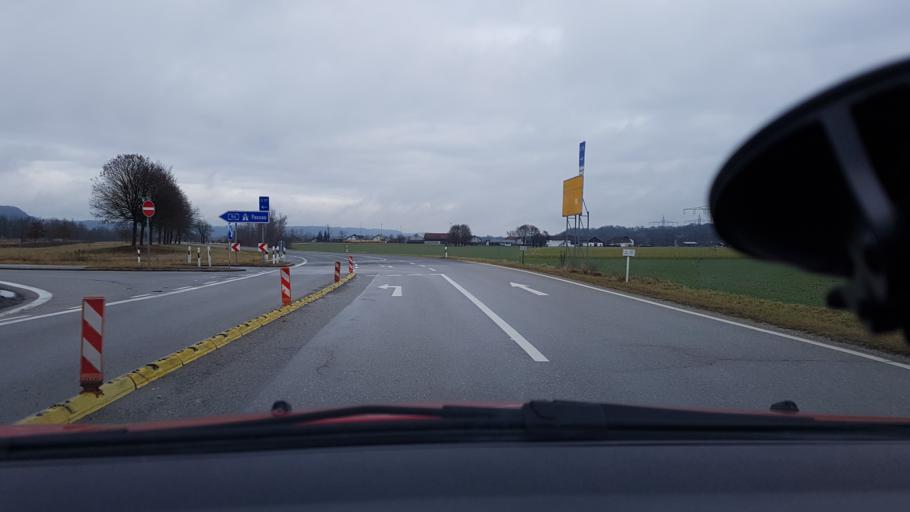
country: DE
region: Bavaria
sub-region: Upper Bavaria
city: Perach
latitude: 48.2468
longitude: 12.7515
